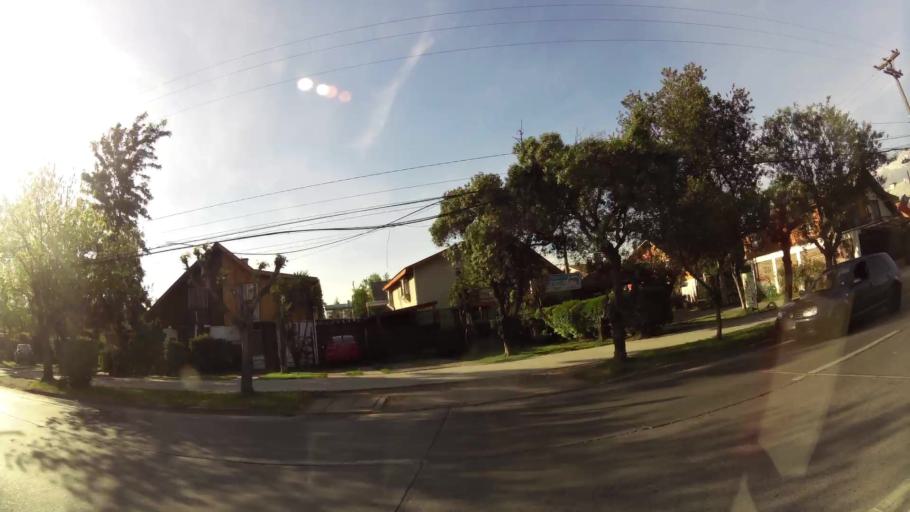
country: CL
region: Santiago Metropolitan
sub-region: Provincia de Cordillera
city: Puente Alto
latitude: -33.5530
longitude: -70.5778
